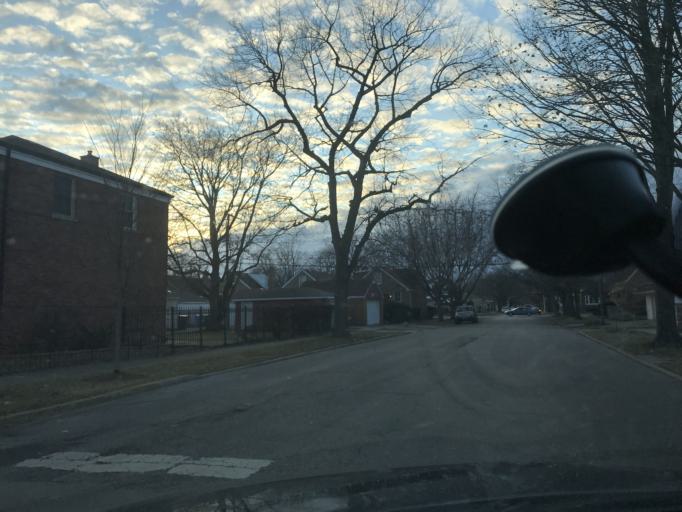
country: US
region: Illinois
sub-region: Cook County
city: Burnham
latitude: 41.7353
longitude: -87.5794
